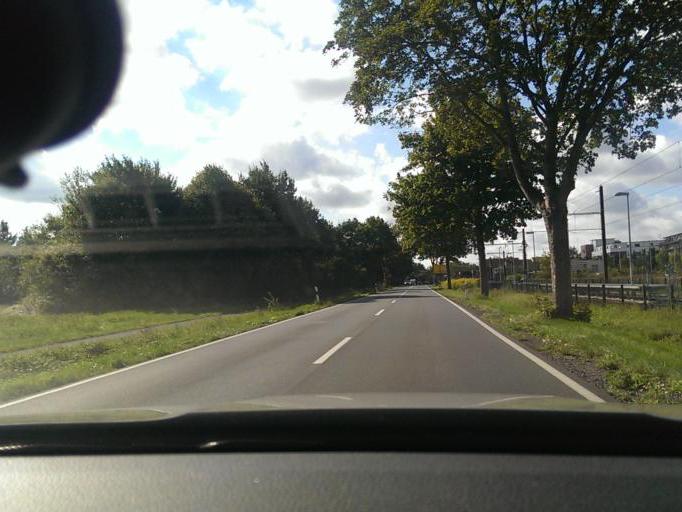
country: DE
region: Lower Saxony
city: Isernhagen Farster Bauerschaft
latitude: 52.4399
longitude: 9.8474
